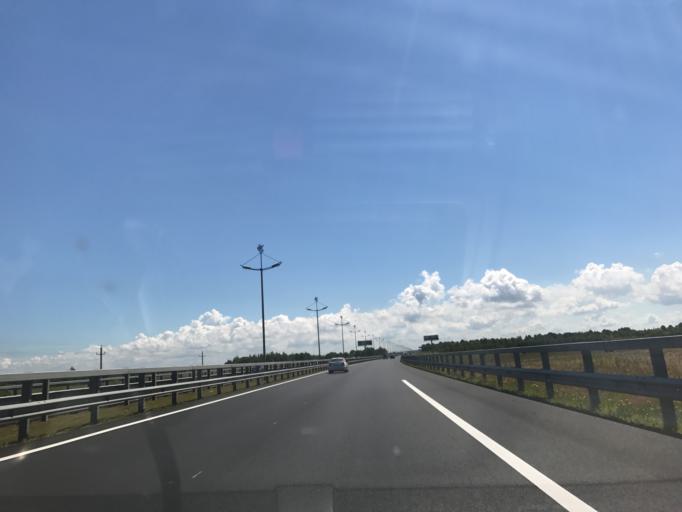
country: RU
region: Kaliningrad
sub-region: Zelenogradskiy Rayon
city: Zelenogradsk
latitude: 54.8925
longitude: 20.5241
